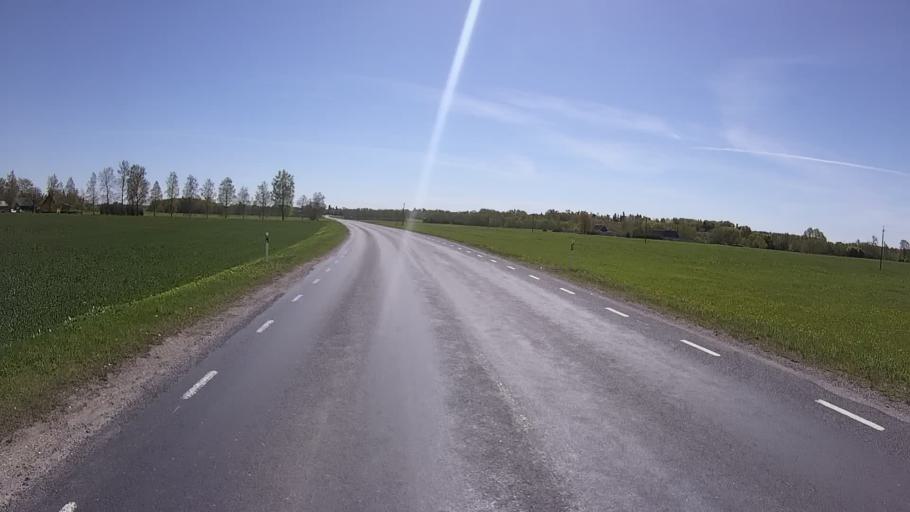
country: EE
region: Harju
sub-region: Raasiku vald
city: Raasiku
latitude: 59.1374
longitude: 25.2018
